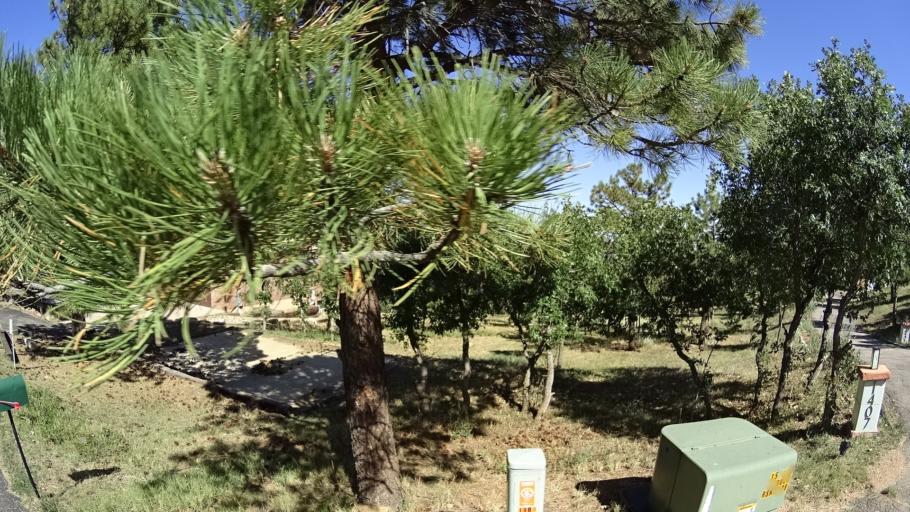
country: US
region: Colorado
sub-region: El Paso County
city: Manitou Springs
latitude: 38.8117
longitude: -104.8788
